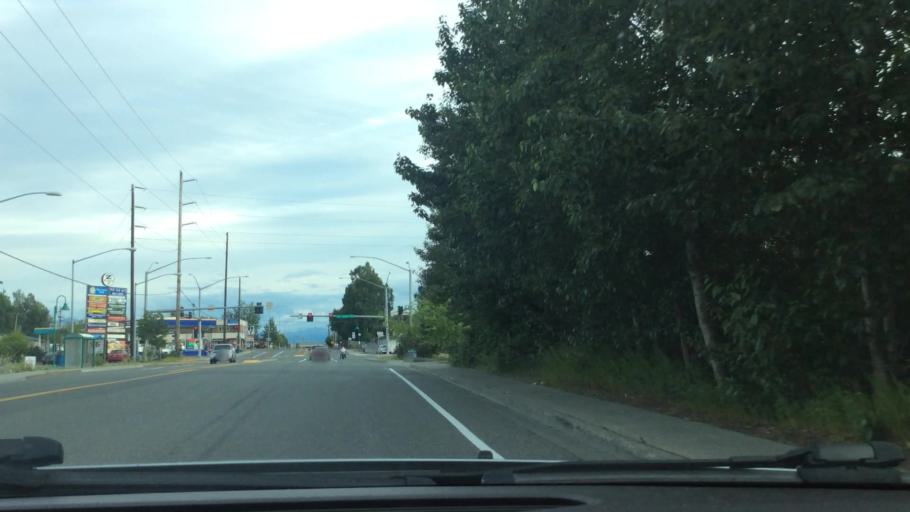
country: US
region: Alaska
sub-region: Anchorage Municipality
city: Anchorage
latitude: 61.1748
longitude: -149.8980
